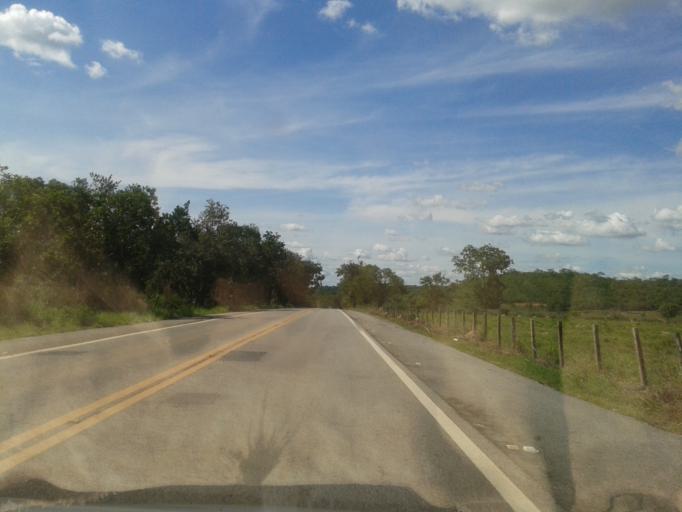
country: BR
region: Goias
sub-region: Itapuranga
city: Itapuranga
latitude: -15.3948
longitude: -50.3854
